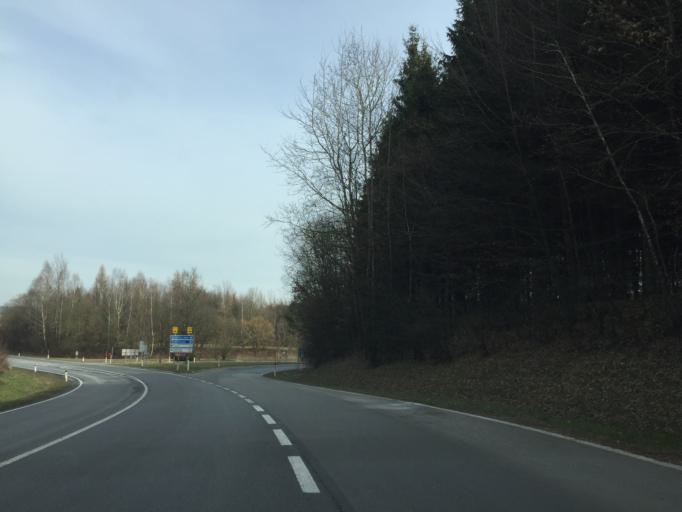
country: AT
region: Upper Austria
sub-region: Politischer Bezirk Ried im Innkreis
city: Ried im Innkreis
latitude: 48.2372
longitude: 13.5098
